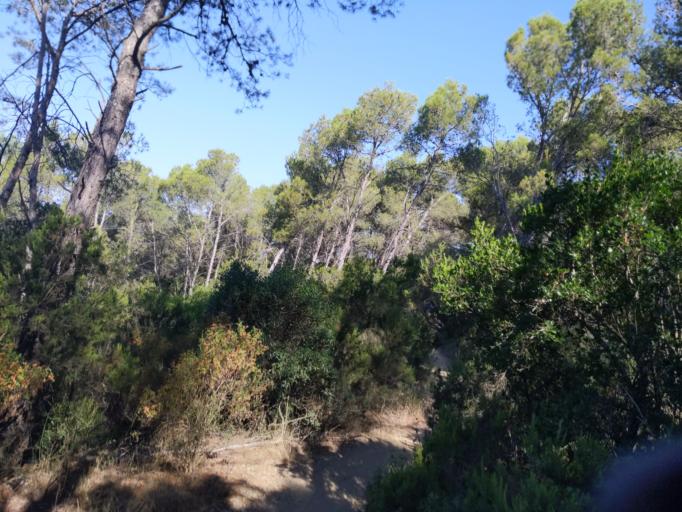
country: ES
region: Catalonia
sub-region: Provincia de Barcelona
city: Cerdanyola del Valles
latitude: 41.4640
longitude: 2.1351
